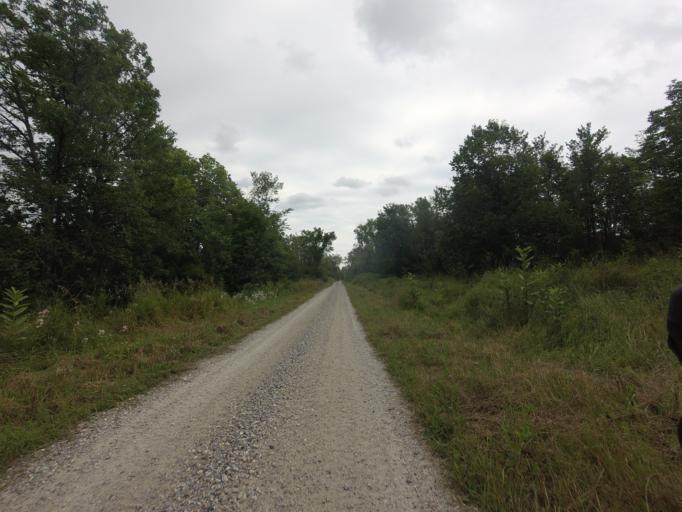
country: CA
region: Ontario
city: Perth
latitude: 44.8216
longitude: -76.5520
